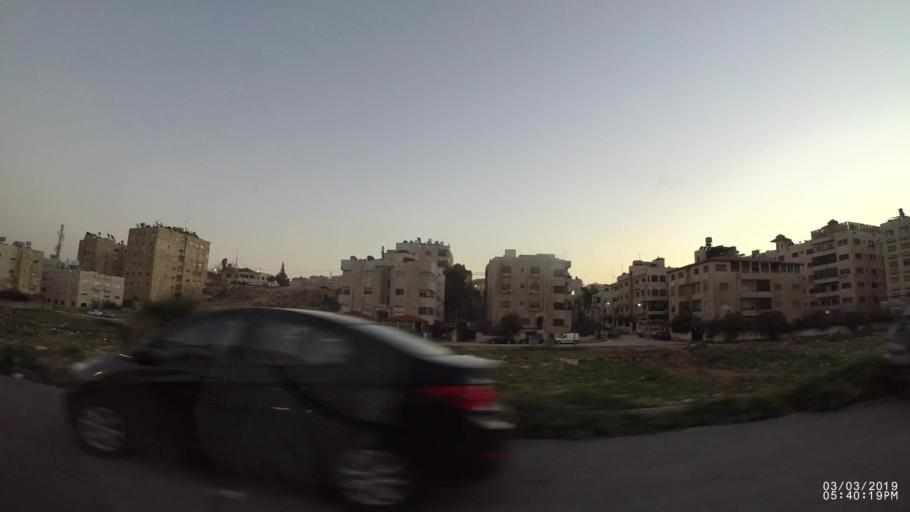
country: JO
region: Amman
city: Al Jubayhah
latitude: 31.9874
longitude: 35.8860
